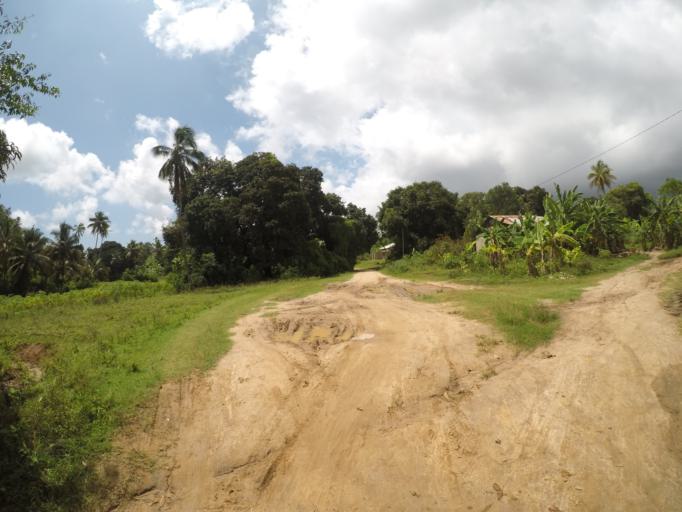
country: TZ
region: Pemba South
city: Mtambile
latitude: -5.3900
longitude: 39.7388
